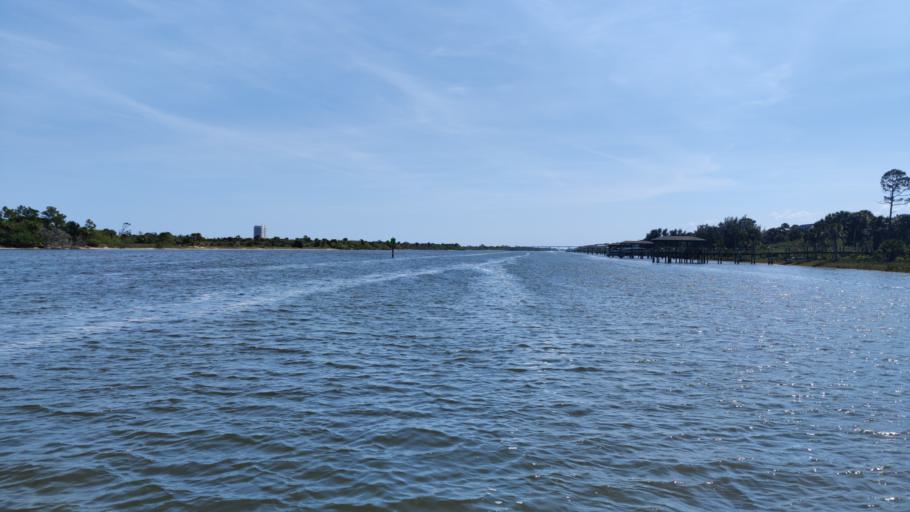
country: US
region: Florida
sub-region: Flagler County
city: Flagler Beach
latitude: 29.5063
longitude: -81.1466
